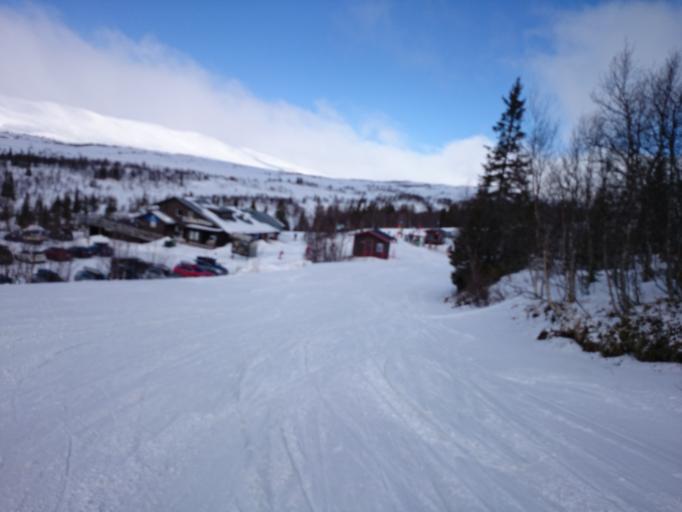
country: SE
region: Jaemtland
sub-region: Are Kommun
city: Are
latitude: 63.4297
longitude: 13.0175
